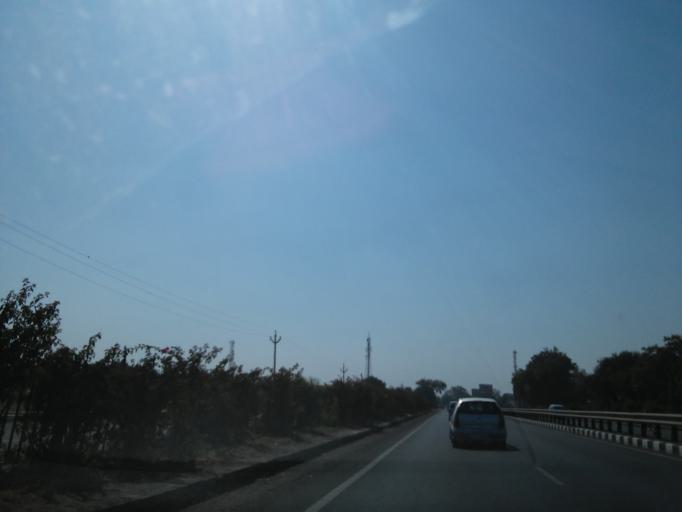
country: IN
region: Gujarat
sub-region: Gandhinagar
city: Chhala
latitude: 23.3421
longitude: 72.7831
